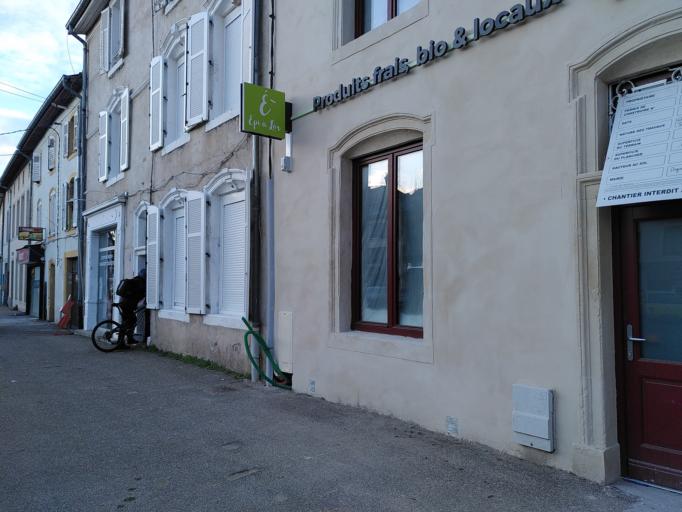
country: FR
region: Lorraine
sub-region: Departement de Meurthe-et-Moselle
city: Pagny-sur-Moselle
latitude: 48.9837
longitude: 6.0211
